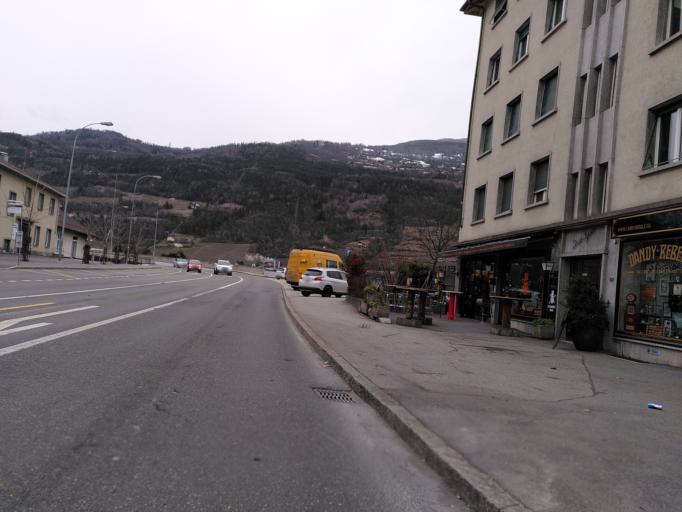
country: CH
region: Valais
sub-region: Sion District
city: Sitten
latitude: 46.2295
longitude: 7.3646
